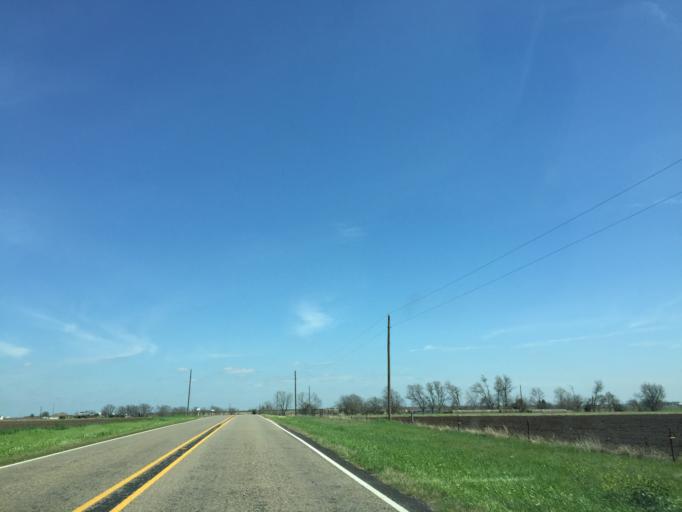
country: US
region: Texas
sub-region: Williamson County
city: Taylor
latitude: 30.5677
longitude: -97.3438
